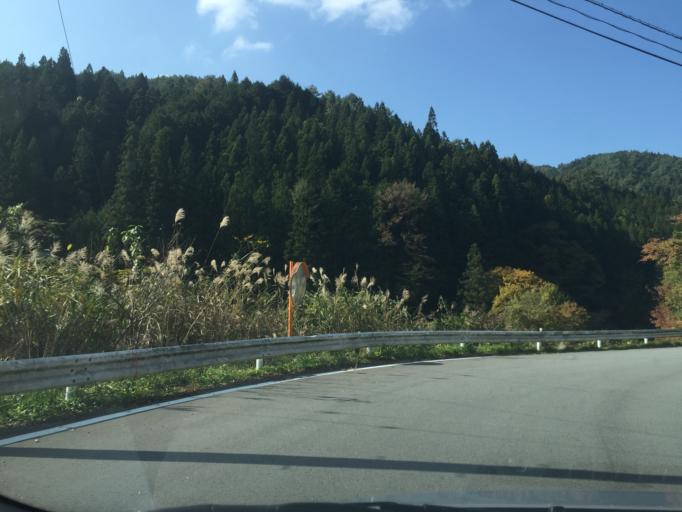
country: JP
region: Gifu
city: Nakatsugawa
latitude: 35.2220
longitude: 137.5940
